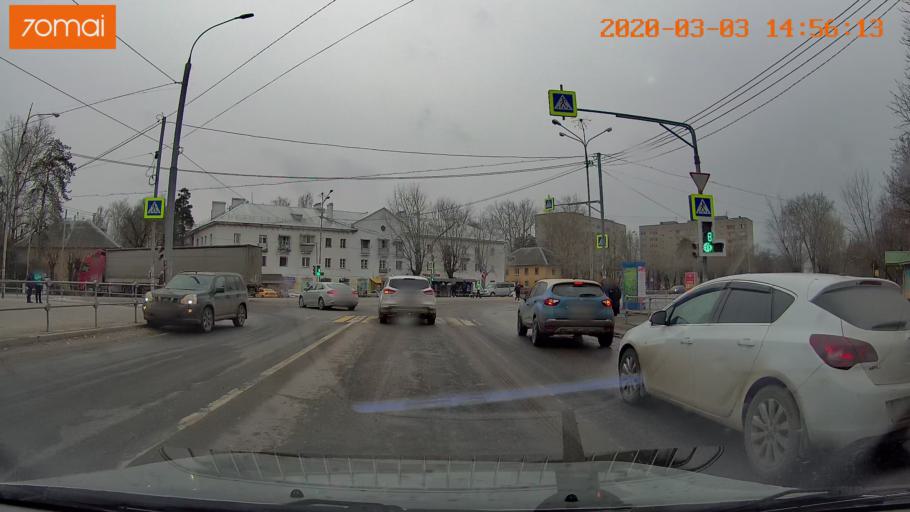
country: RU
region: Moskovskaya
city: Korenevo
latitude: 55.6627
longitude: 37.9971
